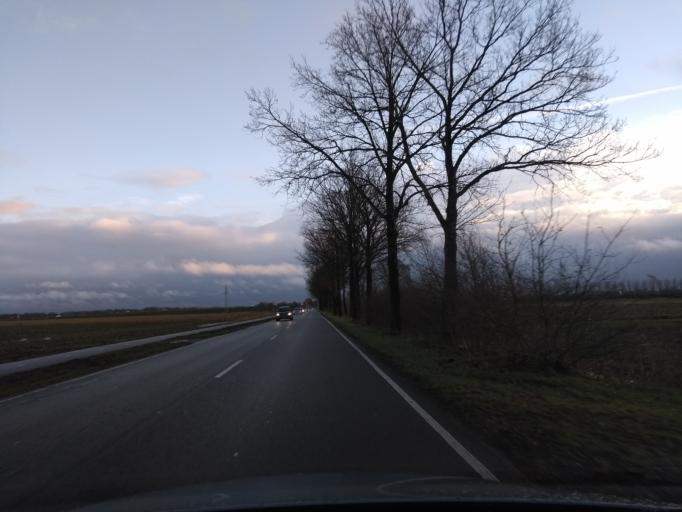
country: NL
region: Overijssel
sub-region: Gemeente Twenterand
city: Vriezenveen
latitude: 52.3930
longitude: 6.6151
